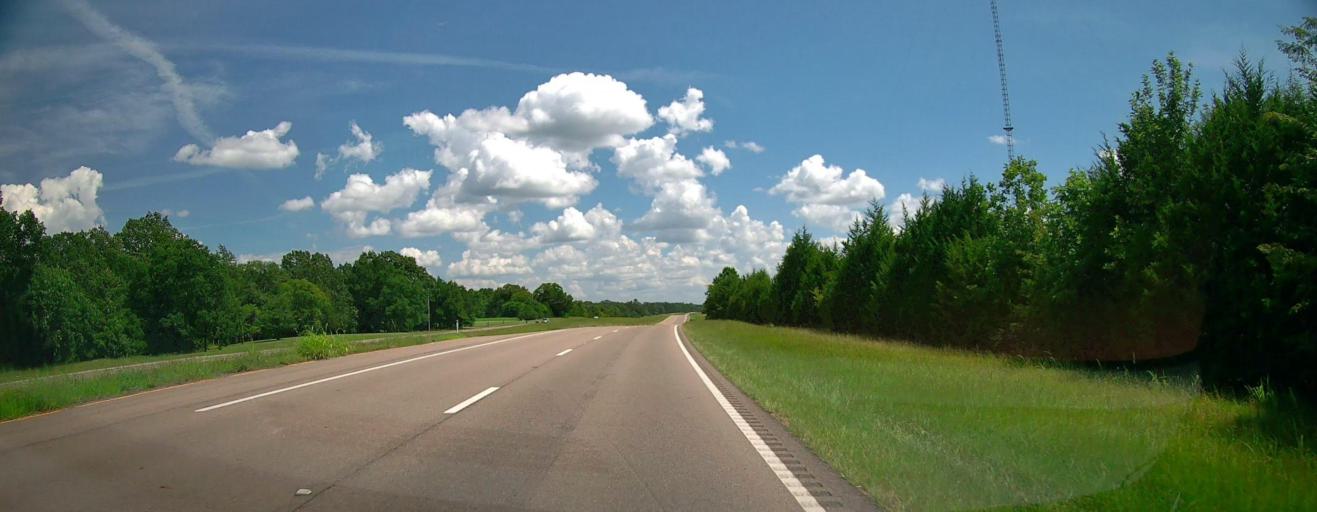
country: US
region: Mississippi
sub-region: Monroe County
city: Amory
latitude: 33.9526
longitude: -88.6044
